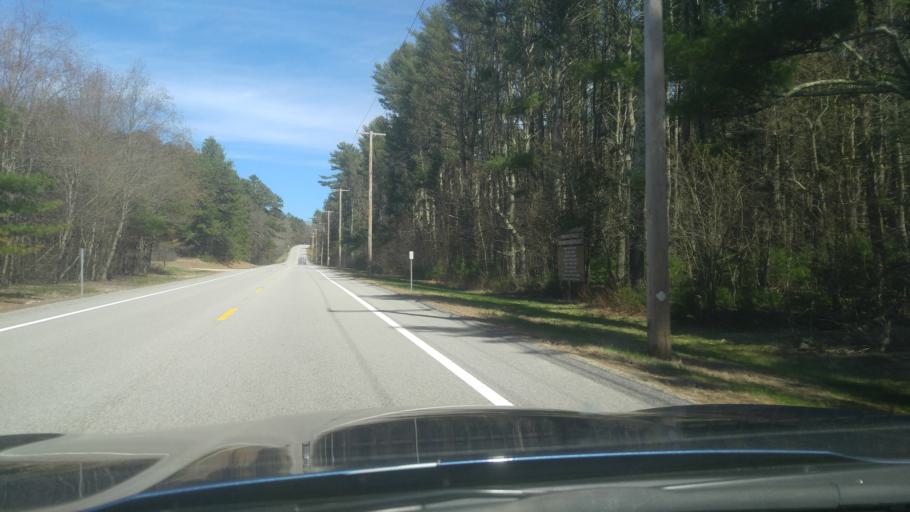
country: US
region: Rhode Island
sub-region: Washington County
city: Hope Valley
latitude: 41.5753
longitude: -71.7159
